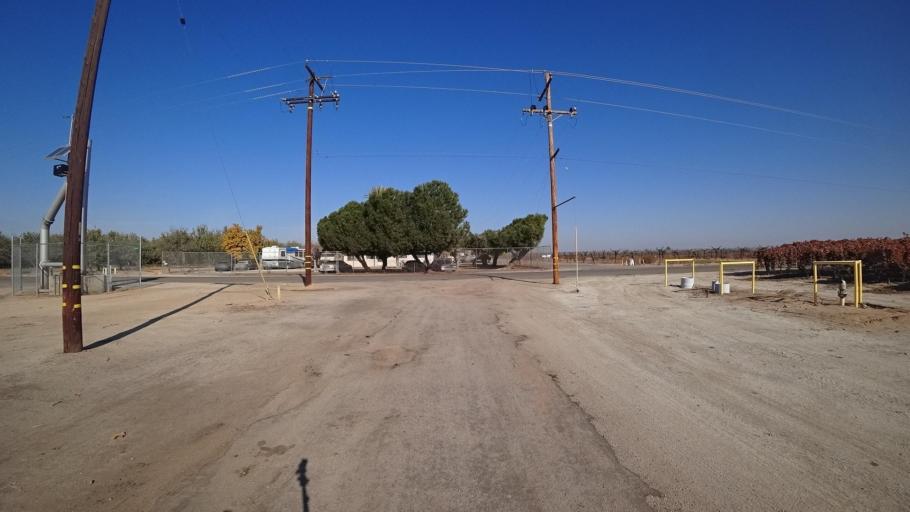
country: US
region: California
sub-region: Kern County
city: Delano
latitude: 35.7466
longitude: -119.2143
